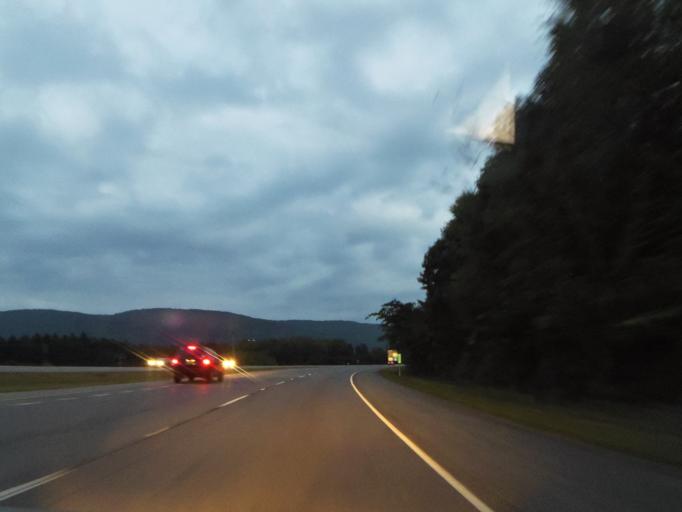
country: US
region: Alabama
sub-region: Madison County
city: New Hope
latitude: 34.6812
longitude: -86.3319
